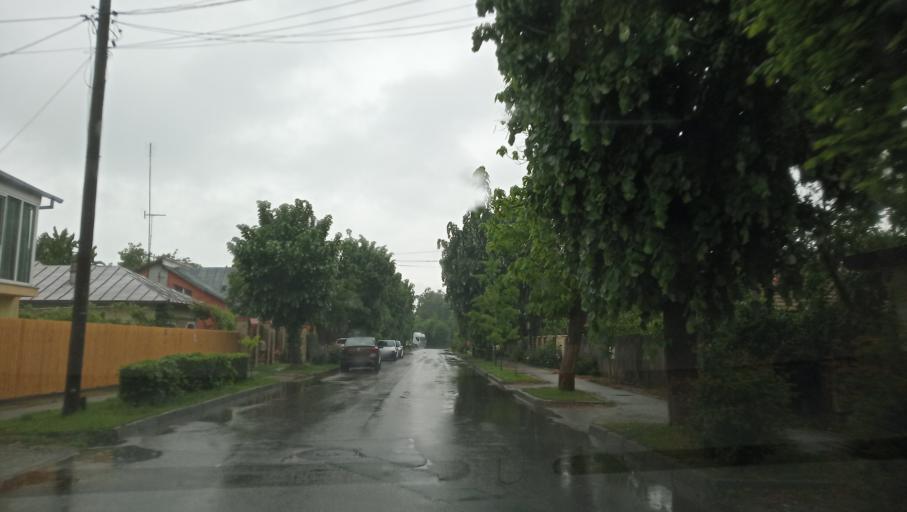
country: RO
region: Dambovita
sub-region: Oras Gaesti
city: Gaesti
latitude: 44.7158
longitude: 25.3153
